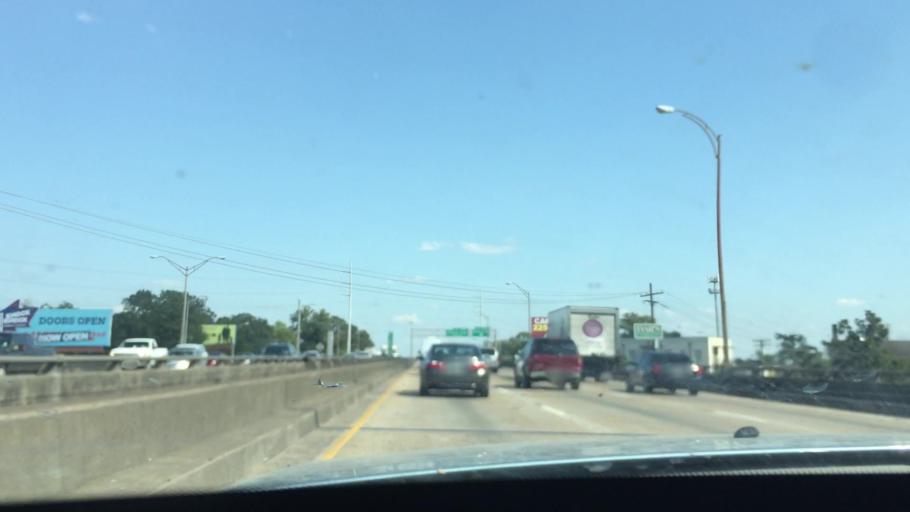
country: US
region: Louisiana
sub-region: East Baton Rouge Parish
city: Baton Rouge
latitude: 30.4250
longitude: -91.1592
